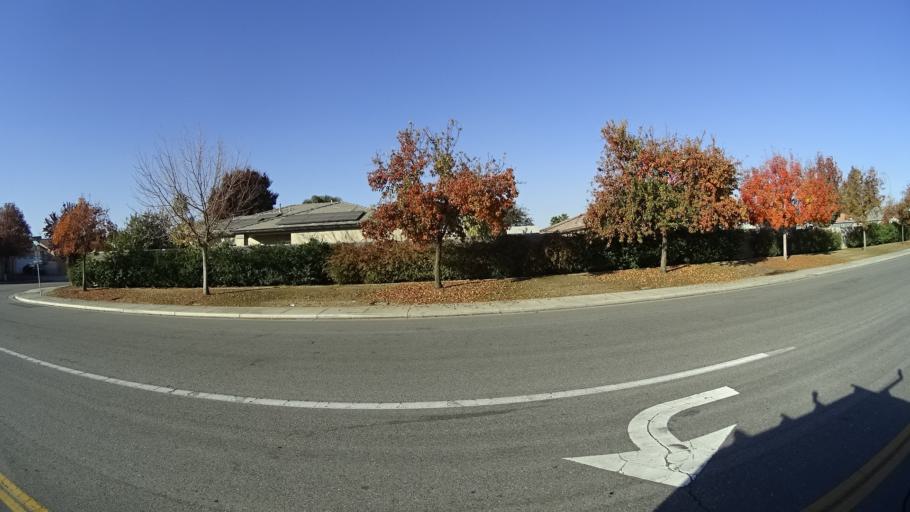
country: US
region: California
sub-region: Kern County
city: Greenfield
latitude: 35.2780
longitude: -119.0301
